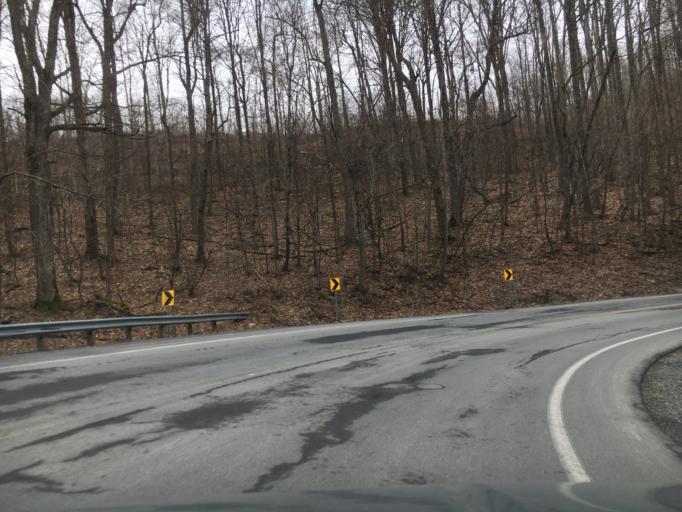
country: US
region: West Virginia
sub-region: Greenbrier County
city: Rainelle
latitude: 37.9871
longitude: -80.8601
